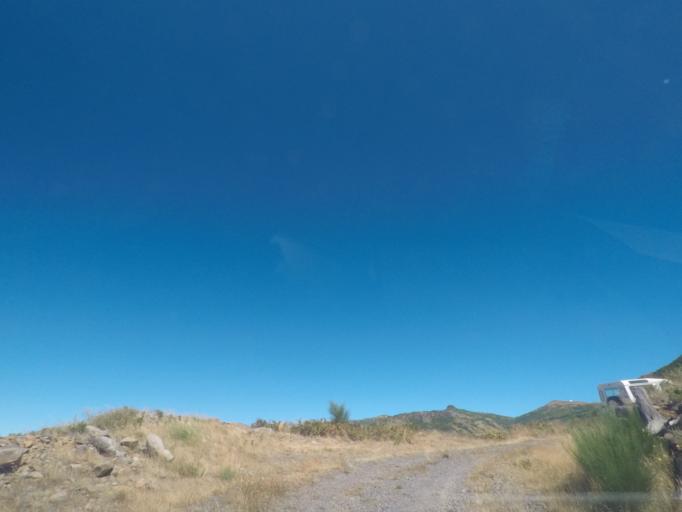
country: PT
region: Madeira
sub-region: Funchal
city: Nossa Senhora do Monte
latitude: 32.7030
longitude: -16.9157
